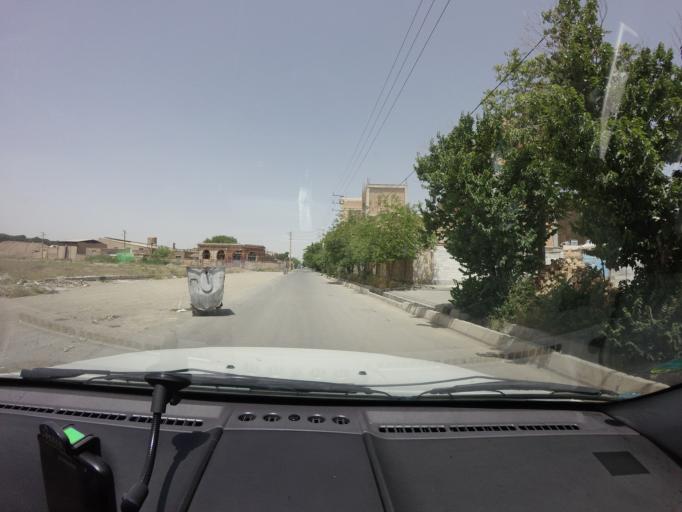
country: IR
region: Tehran
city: Eslamshahr
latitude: 35.5263
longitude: 51.2192
